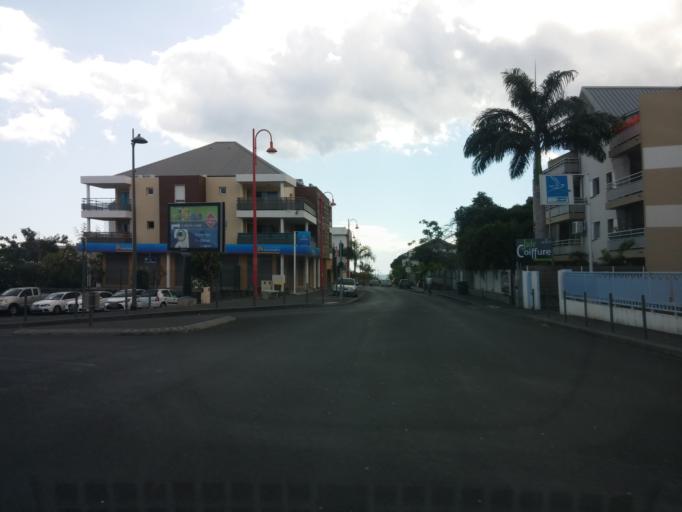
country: RE
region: Reunion
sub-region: Reunion
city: La Possession
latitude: -20.9325
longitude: 55.3350
